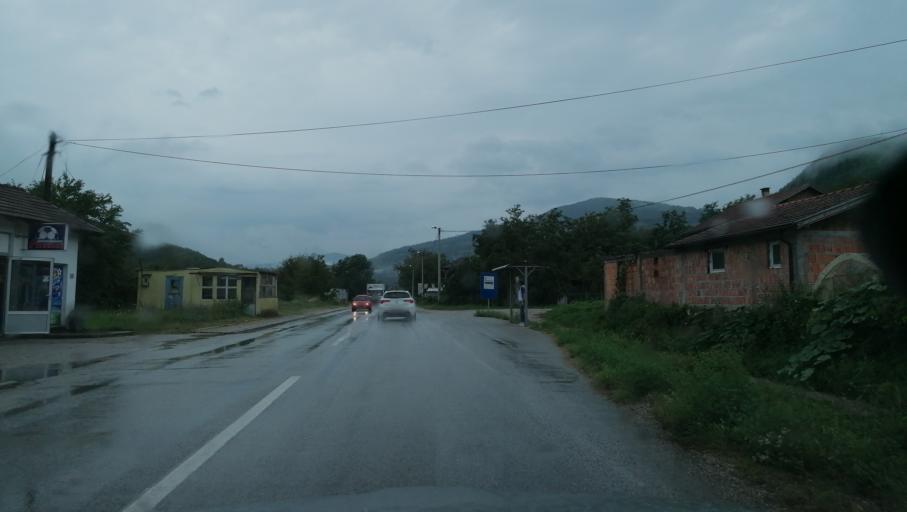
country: BA
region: Federation of Bosnia and Herzegovina
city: Gorazde
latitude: 43.6781
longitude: 19.0198
